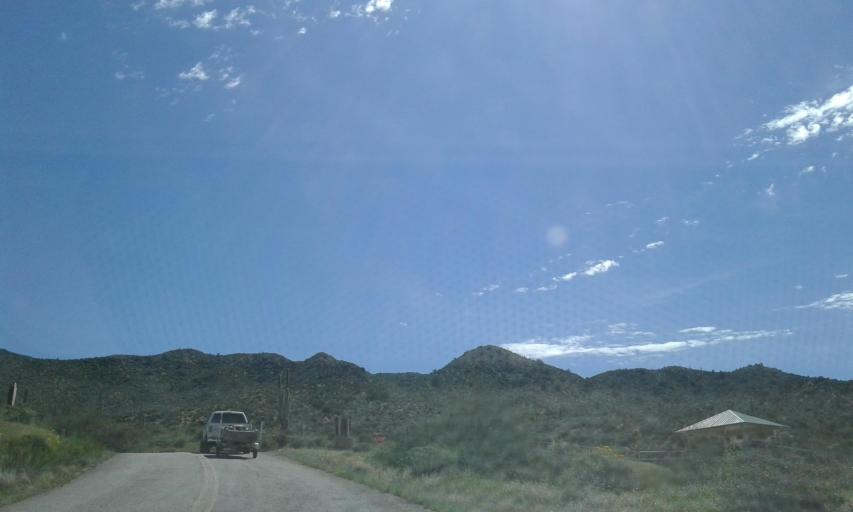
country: US
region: Arizona
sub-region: Gila County
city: Tonto Basin
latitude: 33.5644
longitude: -111.2406
